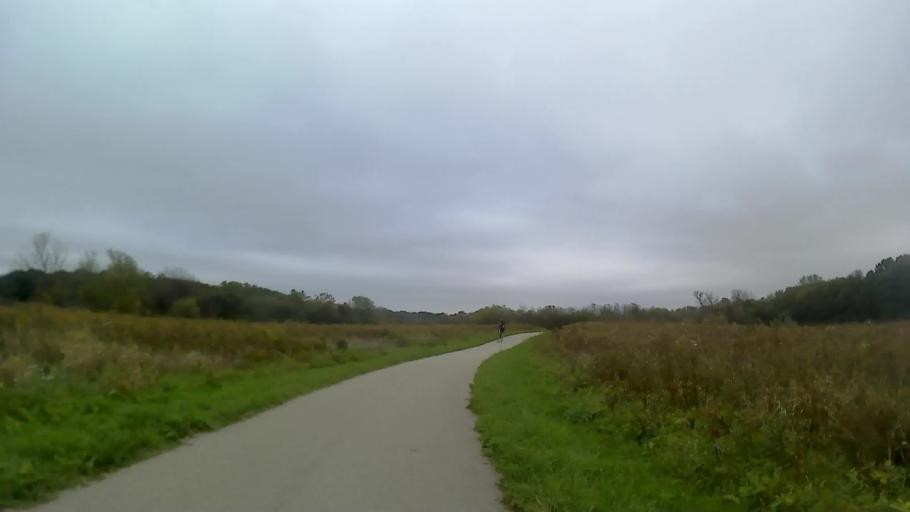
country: US
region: Illinois
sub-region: Kane County
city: Sugar Grove
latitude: 41.7913
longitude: -88.4510
